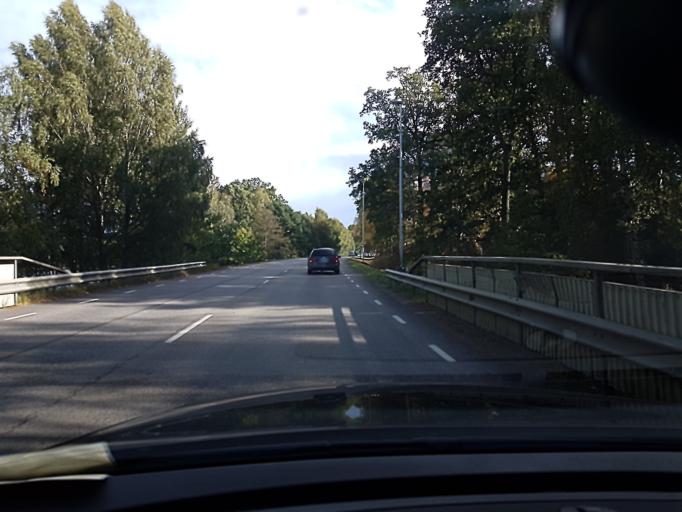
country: SE
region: Kronoberg
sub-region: Vaxjo Kommun
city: Vaexjoe
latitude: 56.8626
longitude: 14.8052
